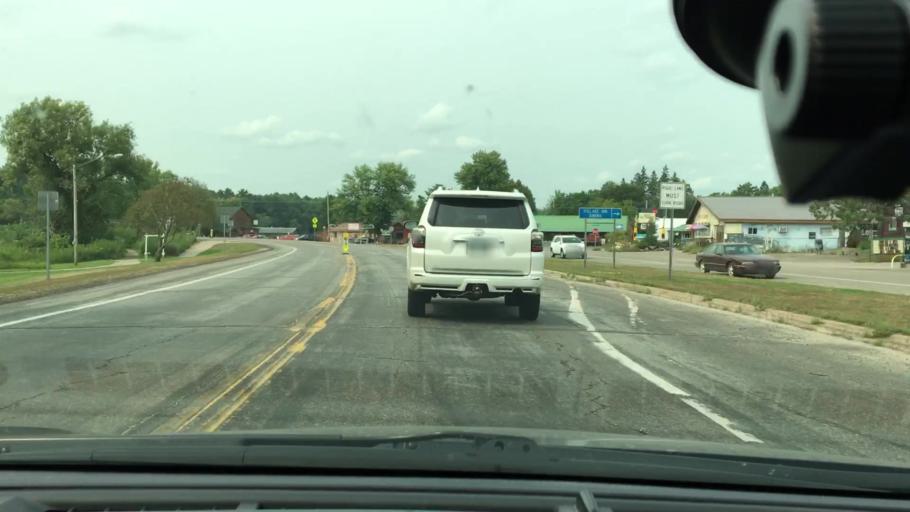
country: US
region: Minnesota
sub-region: Crow Wing County
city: Cross Lake
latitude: 46.8180
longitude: -93.9427
